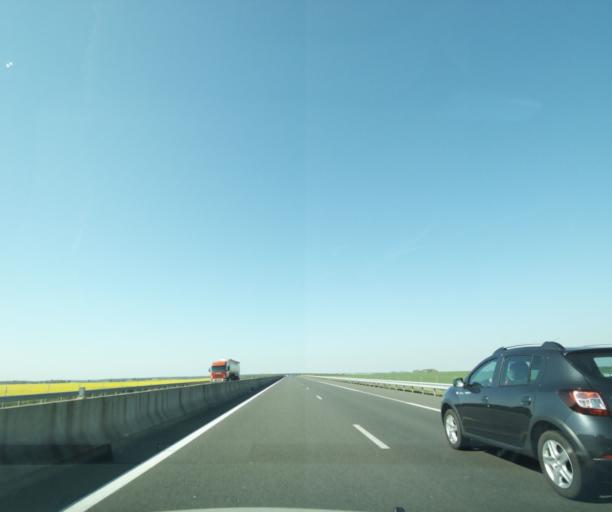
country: FR
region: Centre
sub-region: Departement du Loiret
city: Artenay
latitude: 48.0587
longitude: 1.9447
